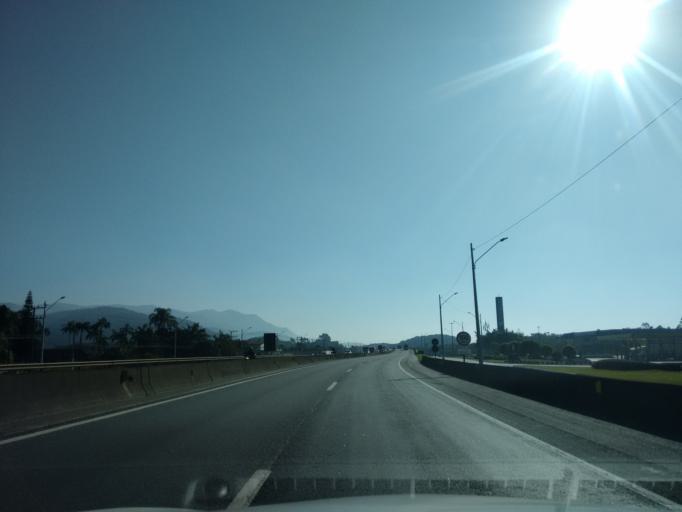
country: BR
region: Santa Catarina
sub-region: Joinville
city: Joinville
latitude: -26.1851
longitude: -48.9112
